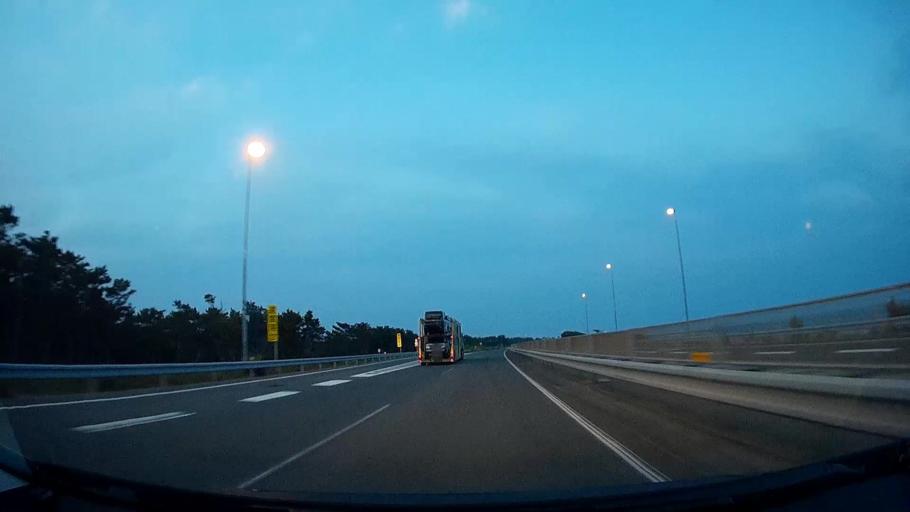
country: JP
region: Shizuoka
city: Kosai-shi
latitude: 34.6810
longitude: 137.5771
